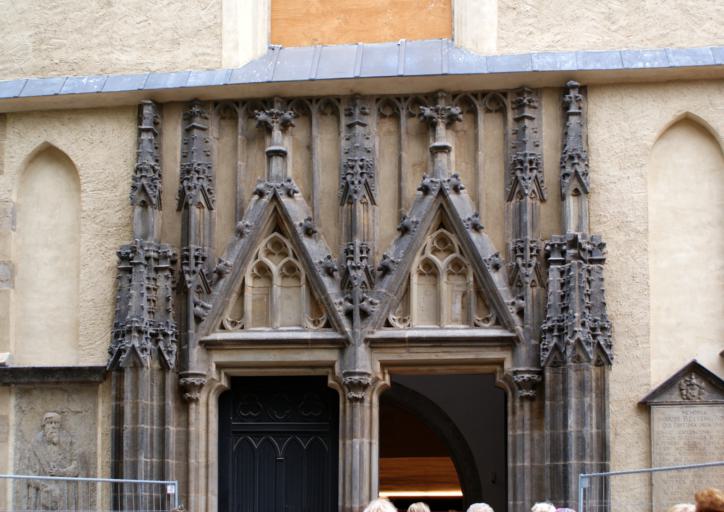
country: DE
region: Saxony-Anhalt
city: Wittenburg
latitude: 51.8664
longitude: 12.6450
